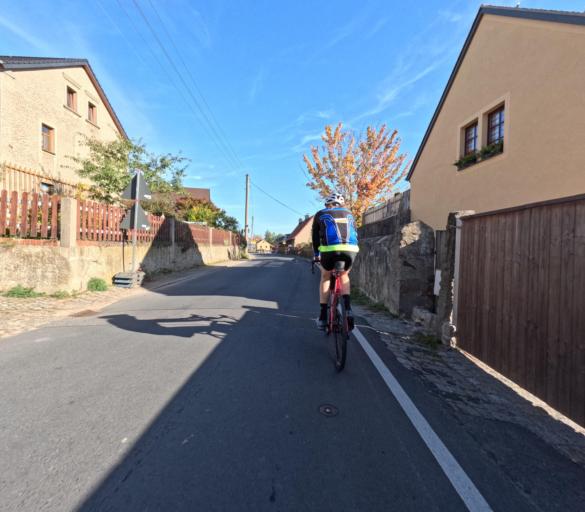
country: DE
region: Saxony
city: Ottendorf-Okrilla
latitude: 51.1341
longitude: 13.8412
